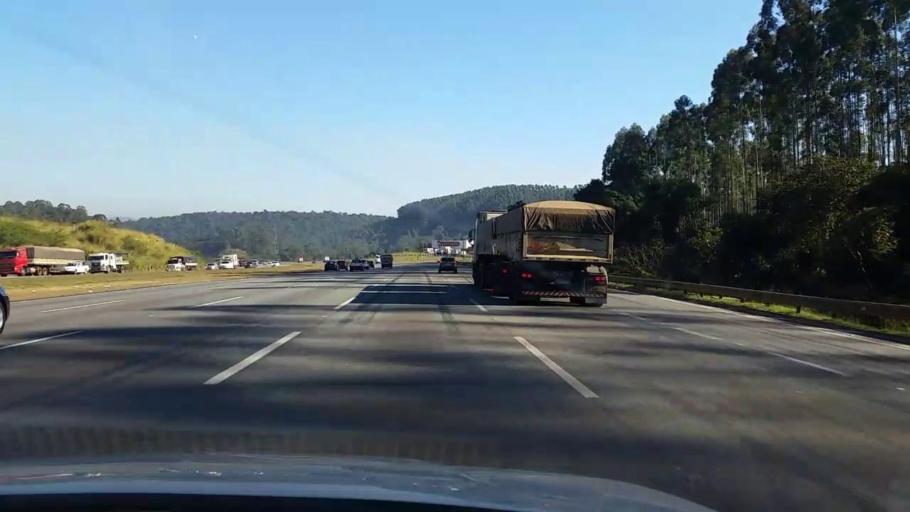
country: BR
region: Sao Paulo
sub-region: Caieiras
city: Caieiras
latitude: -23.3541
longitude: -46.7939
